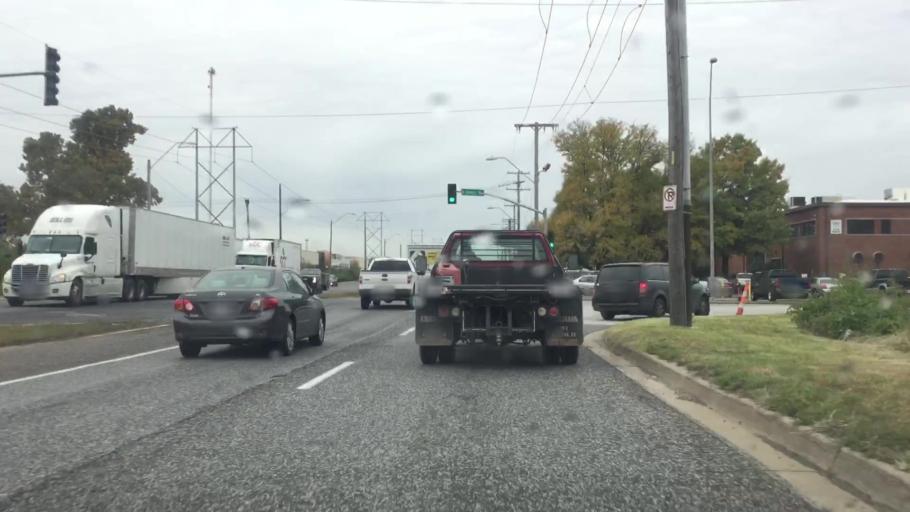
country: US
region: Missouri
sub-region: Clay County
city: North Kansas City
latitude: 39.1306
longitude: -94.5138
